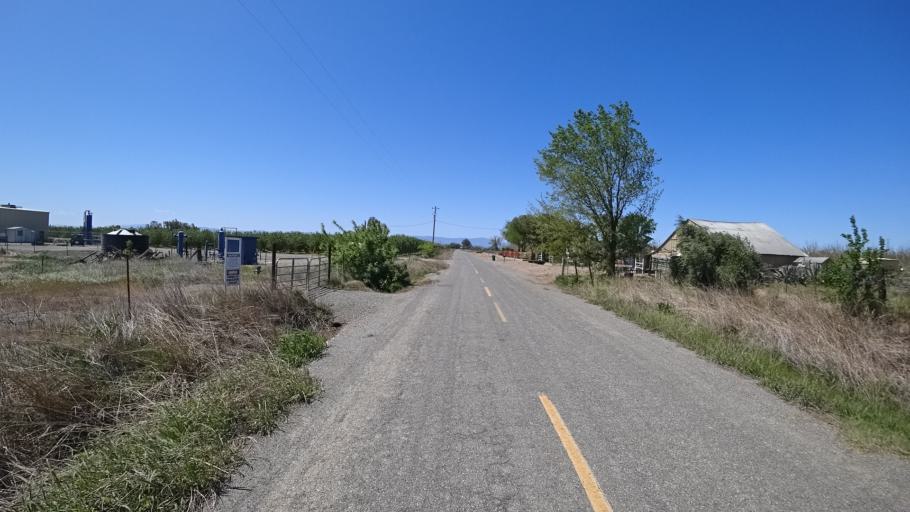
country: US
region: California
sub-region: Glenn County
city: Orland
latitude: 39.7947
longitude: -122.2112
